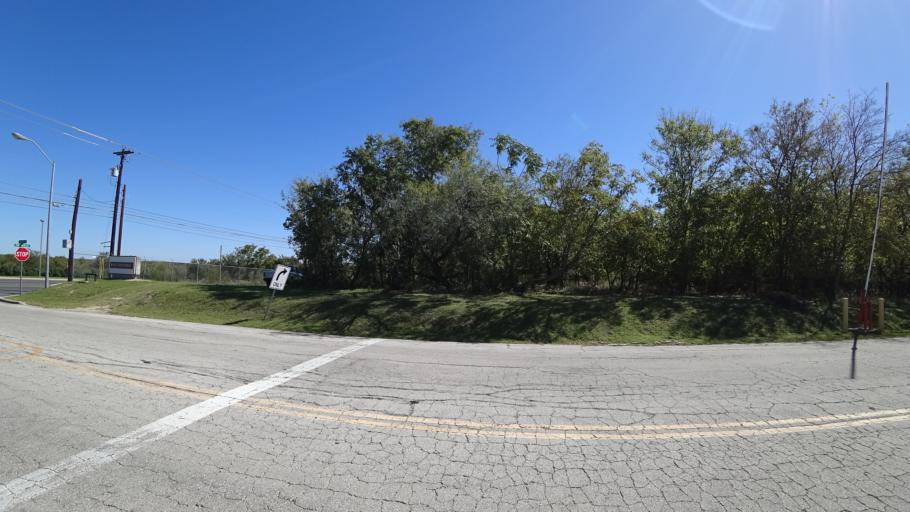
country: US
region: Texas
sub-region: Travis County
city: Hornsby Bend
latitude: 30.2840
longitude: -97.6580
